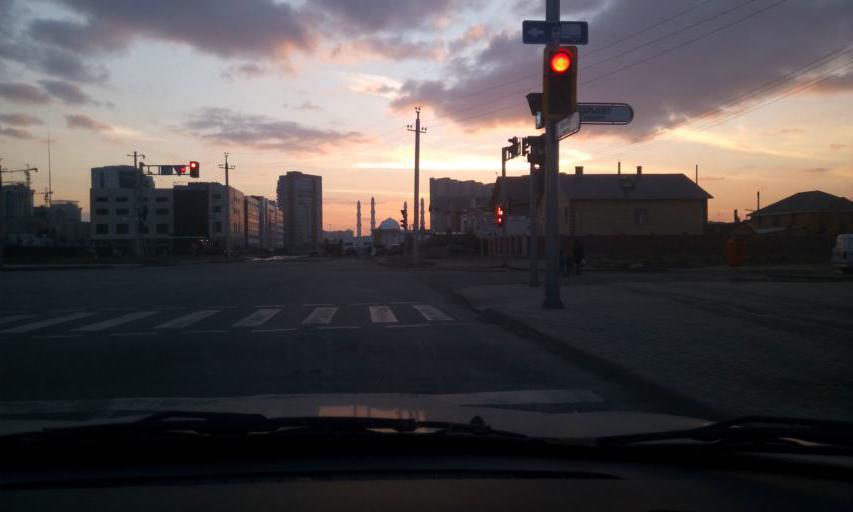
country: KZ
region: Astana Qalasy
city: Astana
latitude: 51.1286
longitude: 71.4854
